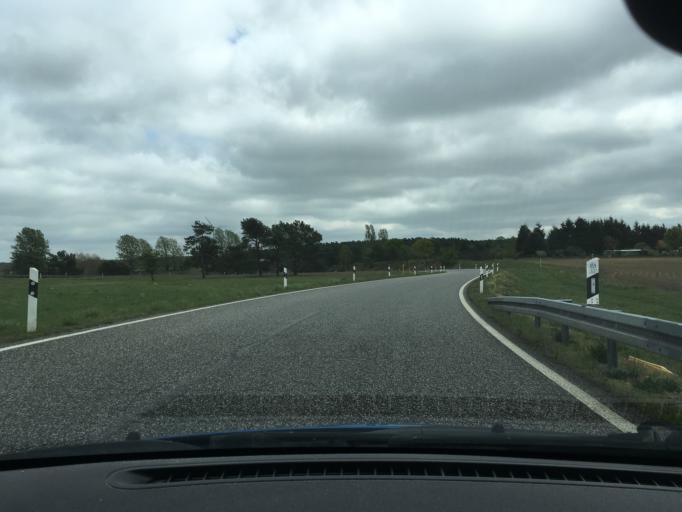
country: DE
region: Mecklenburg-Vorpommern
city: Wittenburg
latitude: 53.4977
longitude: 11.0911
